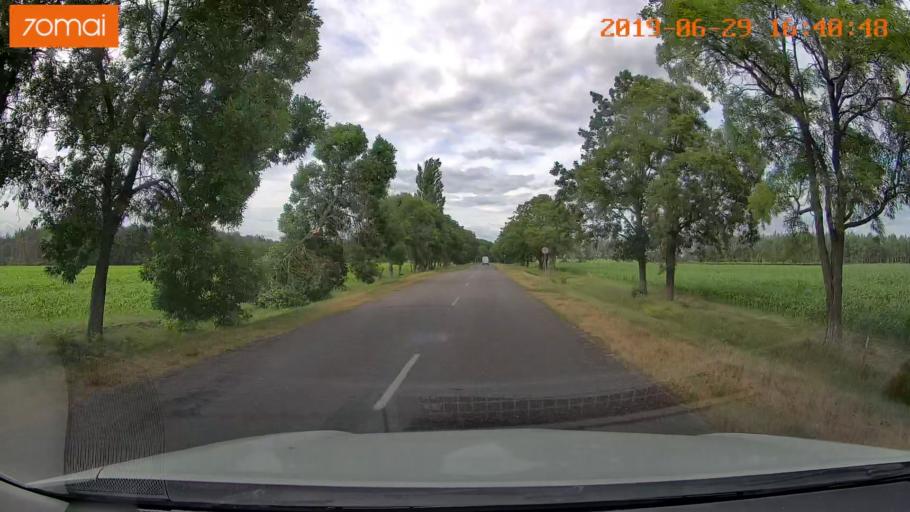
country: BY
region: Brest
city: Luninyets
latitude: 52.2611
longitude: 27.0175
